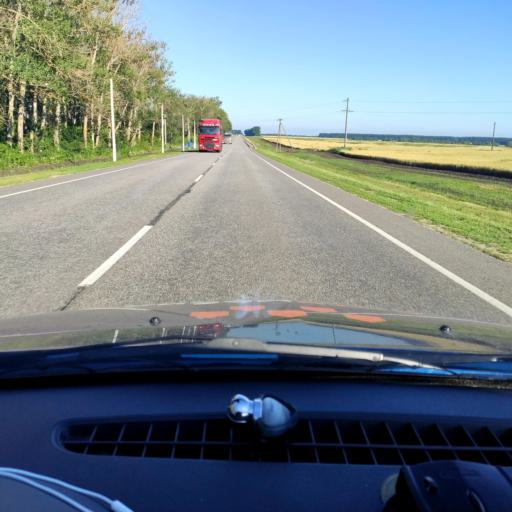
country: RU
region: Orjol
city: Pokrovskoye
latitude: 52.6300
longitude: 36.7043
